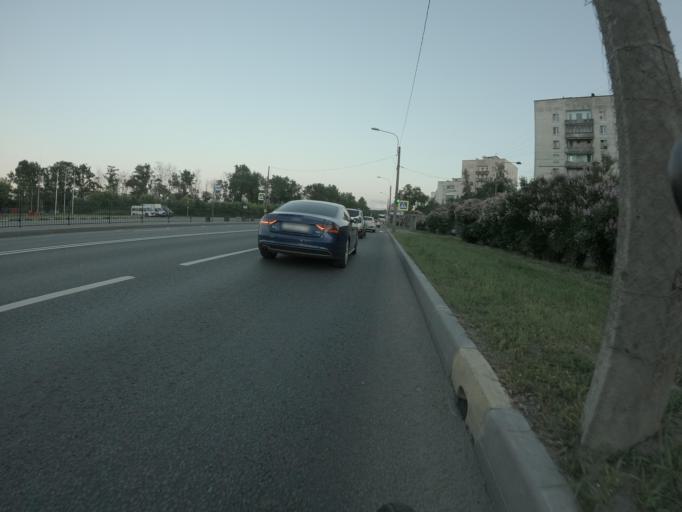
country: RU
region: St.-Petersburg
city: Dachnoye
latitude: 59.8480
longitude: 30.2803
